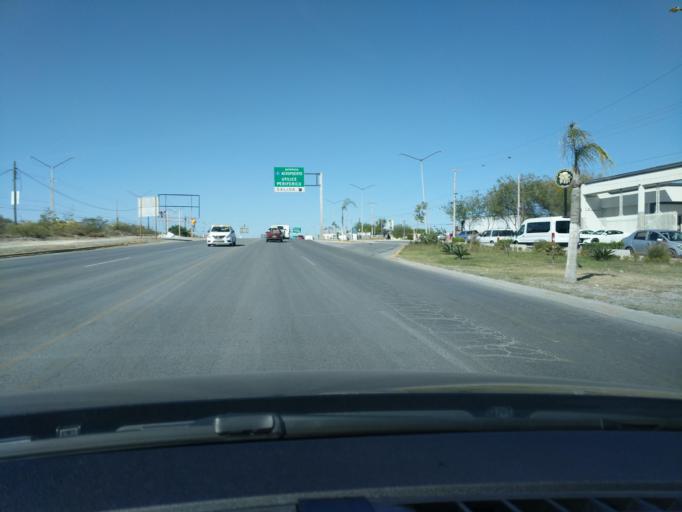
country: MX
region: Nuevo Leon
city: Juarez
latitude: 25.6555
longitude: -100.0805
